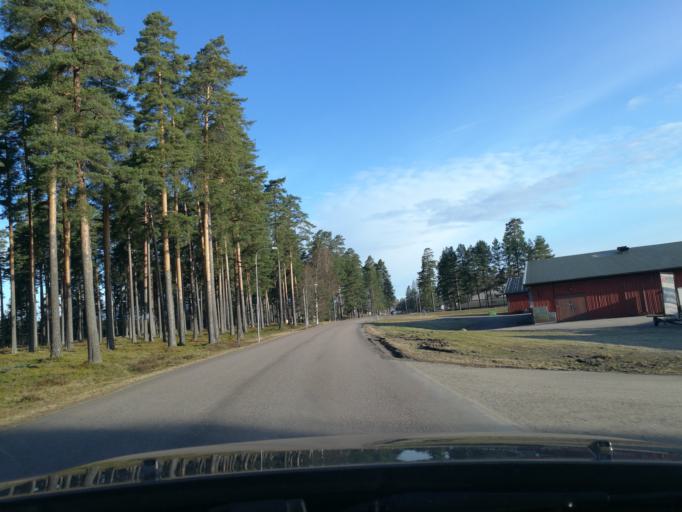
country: SE
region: Vaermland
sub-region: Eda Kommun
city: Charlottenberg
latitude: 59.8777
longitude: 12.2849
